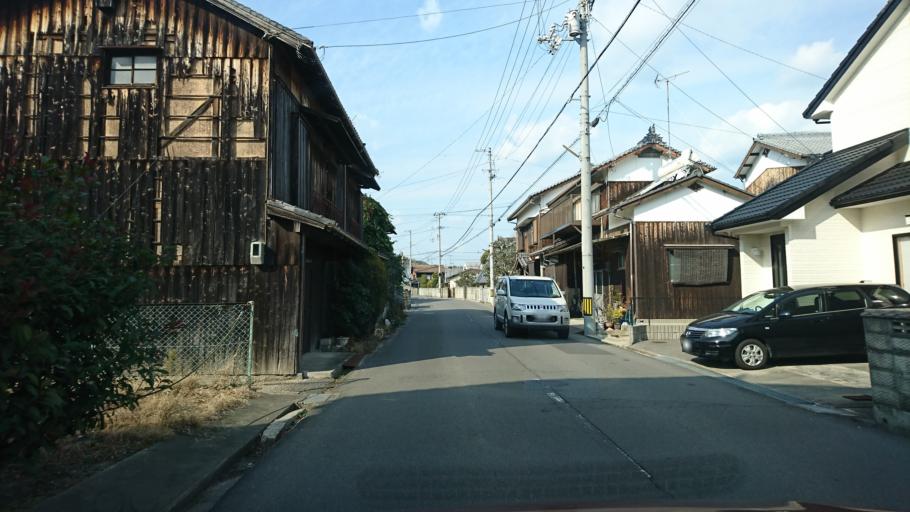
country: JP
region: Ehime
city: Saijo
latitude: 34.0200
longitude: 133.0407
